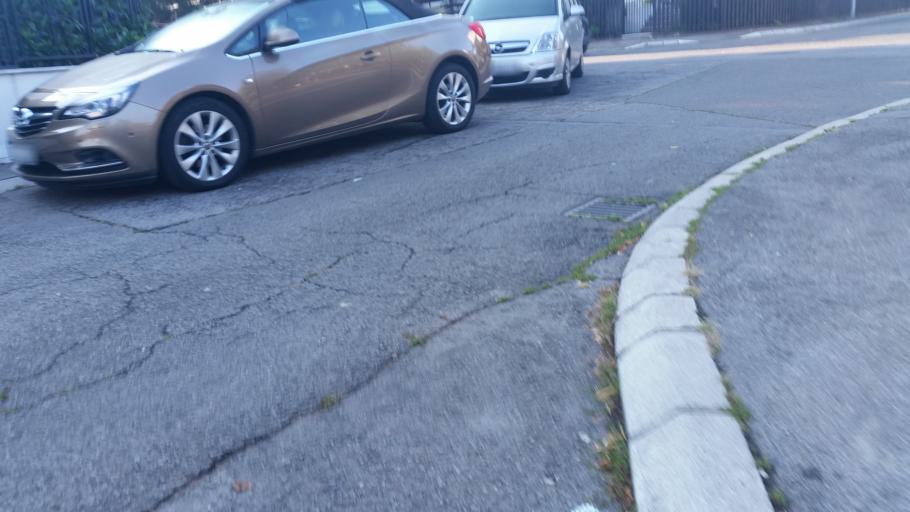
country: RS
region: Central Serbia
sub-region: Belgrade
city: Zemun
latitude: 44.8182
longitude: 20.3915
